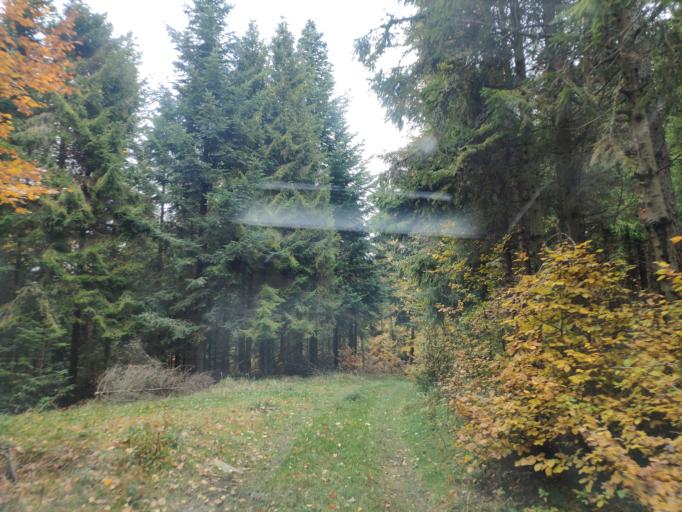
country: SK
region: Kosicky
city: Medzev
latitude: 48.7406
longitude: 20.9914
